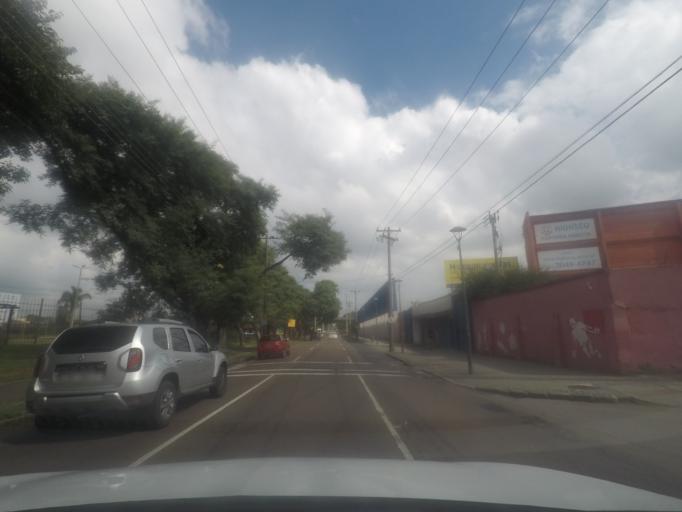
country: BR
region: Parana
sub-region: Curitiba
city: Curitiba
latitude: -25.4400
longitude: -49.2547
